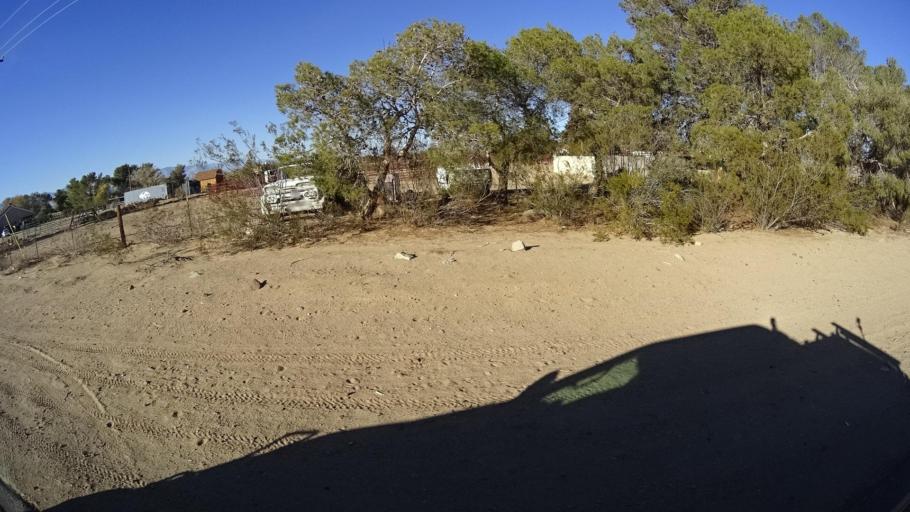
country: US
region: California
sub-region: Kern County
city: Ridgecrest
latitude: 35.6297
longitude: -117.7107
